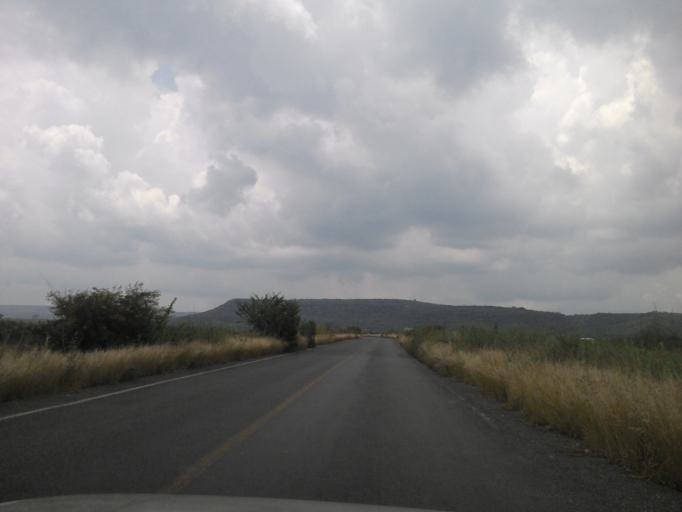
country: MX
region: Jalisco
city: San Diego de Alejandria
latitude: 20.8915
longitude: -101.9683
